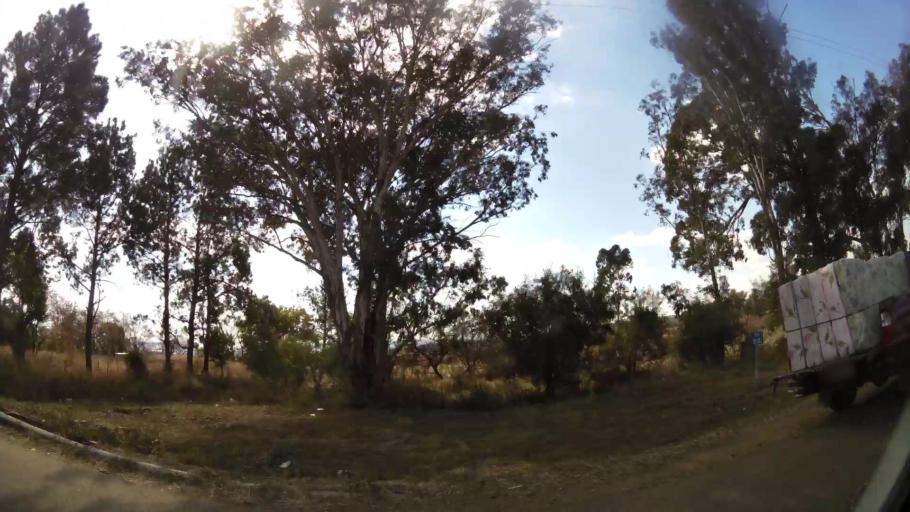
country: ZA
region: Gauteng
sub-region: City of Tshwane Metropolitan Municipality
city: Cullinan
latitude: -25.7501
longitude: 28.3670
